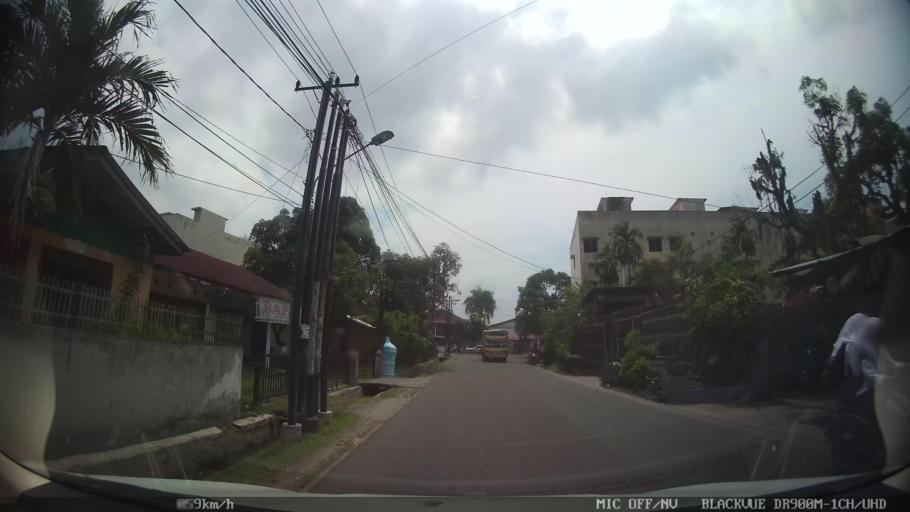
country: ID
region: North Sumatra
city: Medan
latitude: 3.6422
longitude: 98.6645
